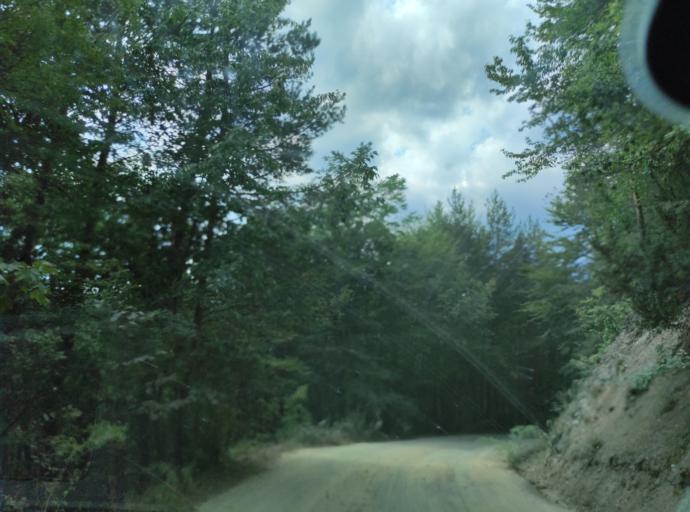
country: BG
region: Blagoevgrad
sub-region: Obshtina Belitsa
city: Belitsa
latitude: 42.0232
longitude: 23.5766
